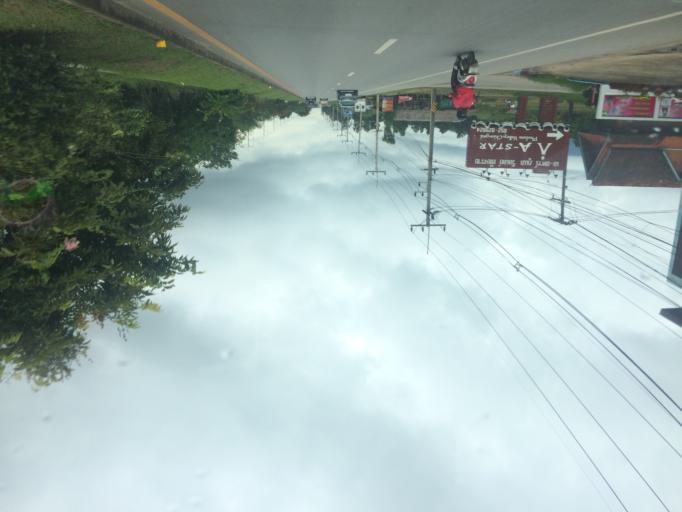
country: TH
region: Chiang Rai
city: Mae Chan
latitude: 20.0576
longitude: 99.8754
